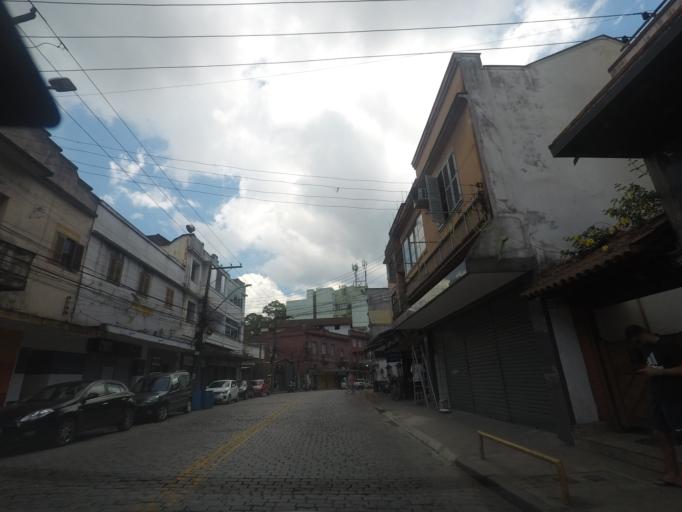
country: BR
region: Rio de Janeiro
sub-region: Petropolis
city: Petropolis
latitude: -22.5049
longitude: -43.1812
